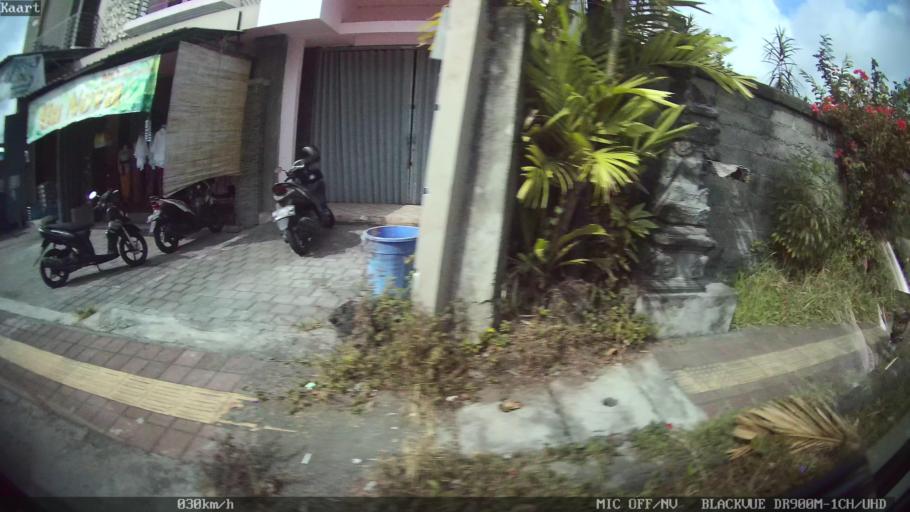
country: ID
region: Bali
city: Banjar Kertasari
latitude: -8.6202
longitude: 115.2051
